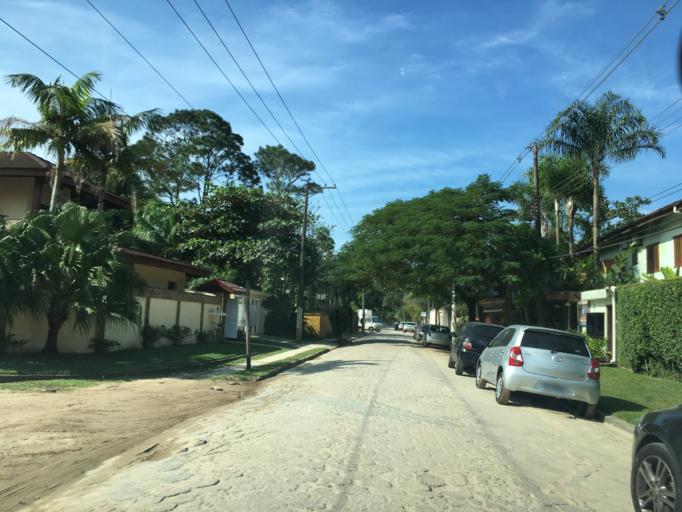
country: BR
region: Sao Paulo
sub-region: Sao Sebastiao
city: Sao Sebastiao
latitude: -23.7671
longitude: -45.7374
